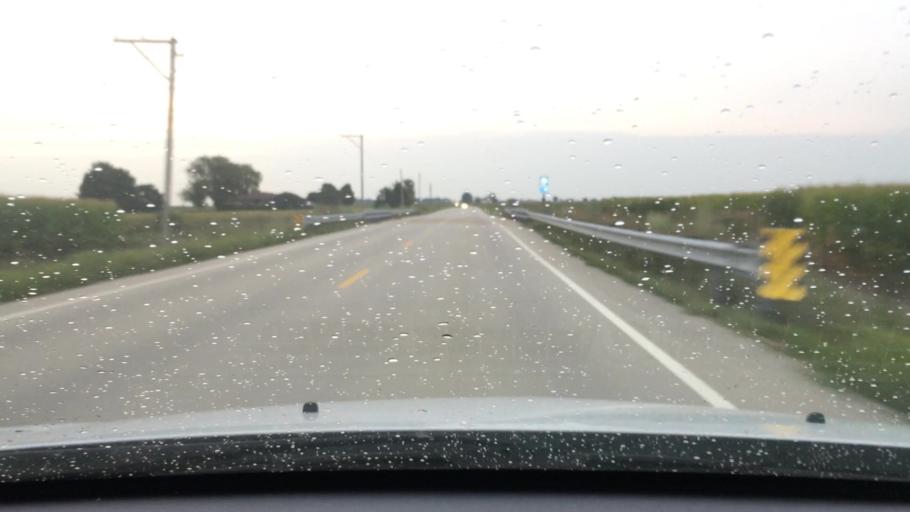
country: US
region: Illinois
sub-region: DeKalb County
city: Malta
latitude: 41.8488
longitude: -88.8218
